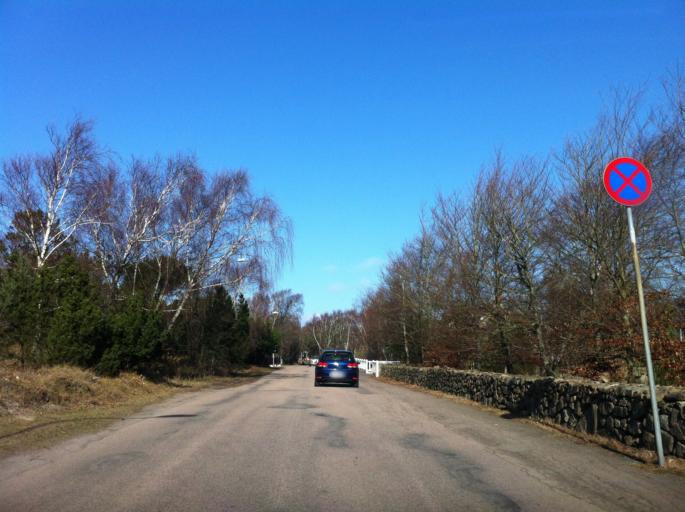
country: SE
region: Skane
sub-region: Angelholms Kommun
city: AEngelholm
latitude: 56.2607
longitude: 12.8363
